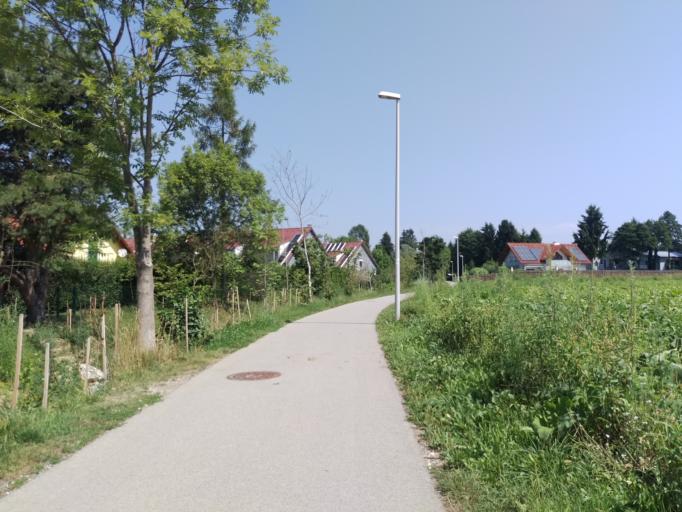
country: AT
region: Styria
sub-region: Graz Stadt
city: Graz
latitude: 47.0452
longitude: 15.4687
